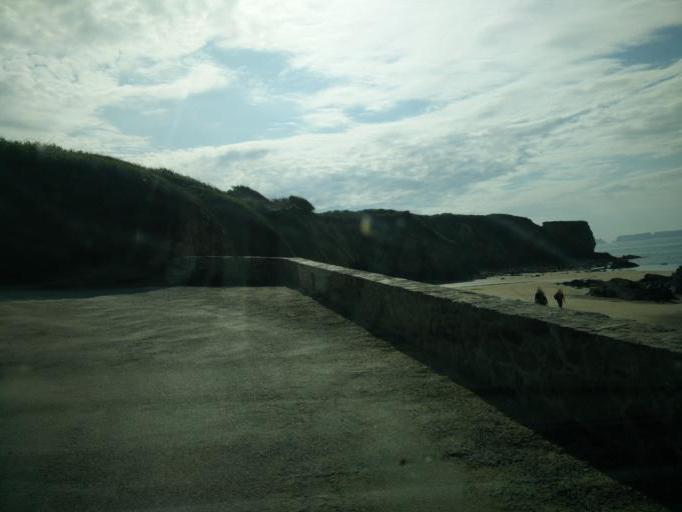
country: FR
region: Brittany
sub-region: Departement du Finistere
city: Crozon
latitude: 48.2403
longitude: -4.5456
